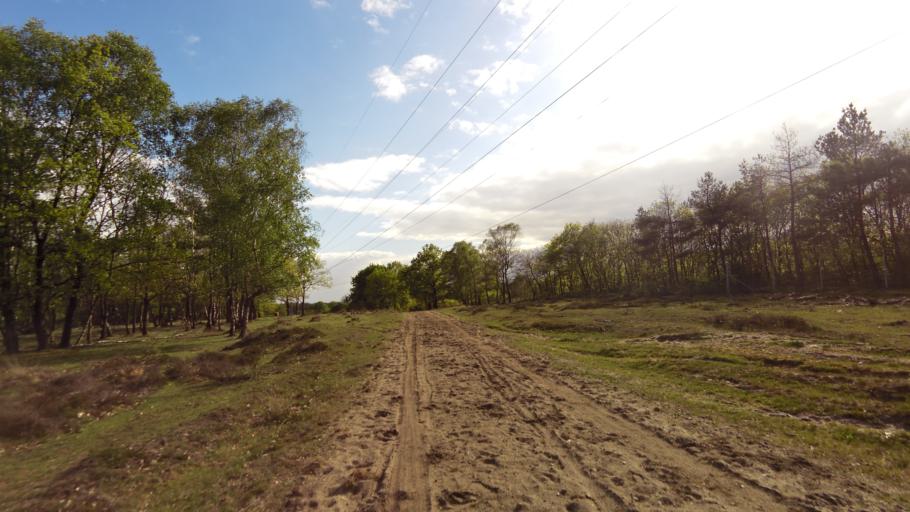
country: NL
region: Gelderland
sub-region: Gemeente Rozendaal
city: Rozendaal
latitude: 52.0633
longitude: 5.9444
